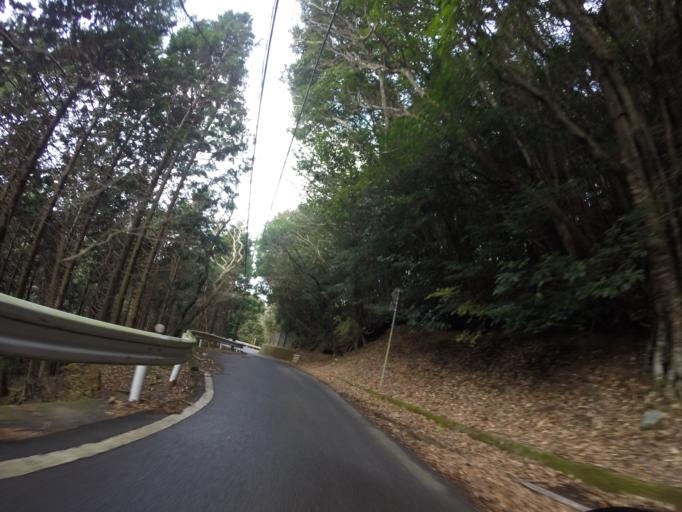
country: JP
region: Shizuoka
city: Heda
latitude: 34.8746
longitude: 138.8587
